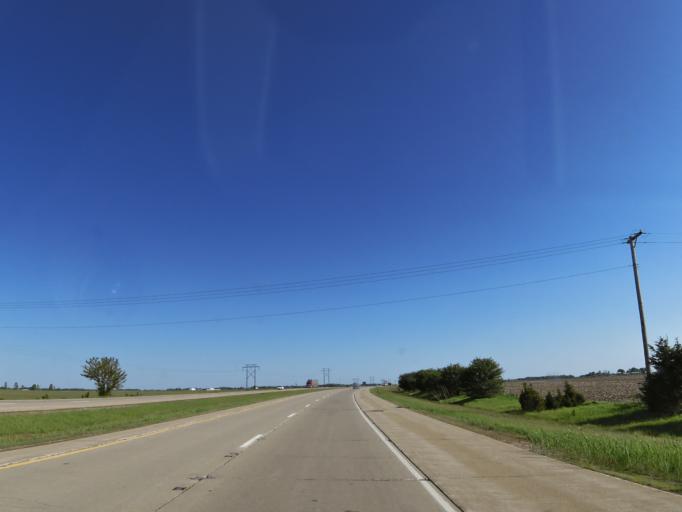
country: US
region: Illinois
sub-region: LaSalle County
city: Oglesby
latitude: 41.2510
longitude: -89.0785
